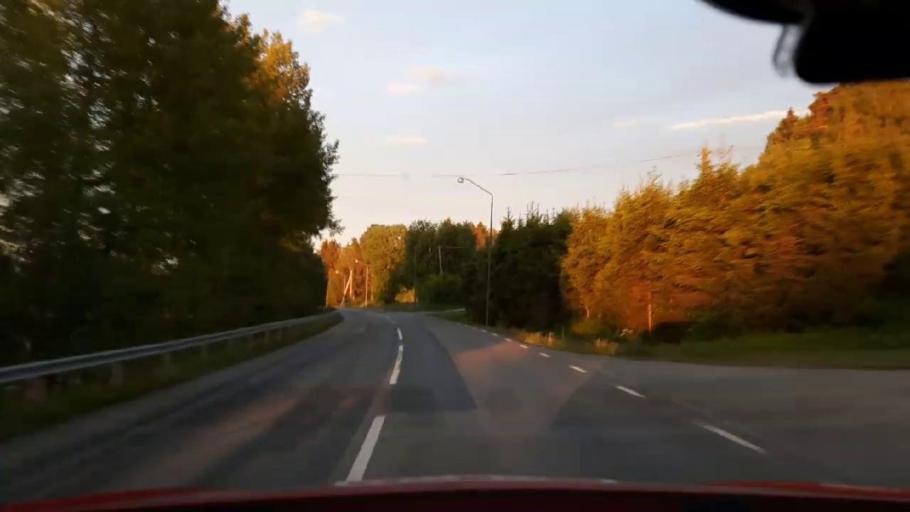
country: SE
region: Jaemtland
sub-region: OEstersunds Kommun
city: Ostersund
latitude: 63.1370
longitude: 14.6346
